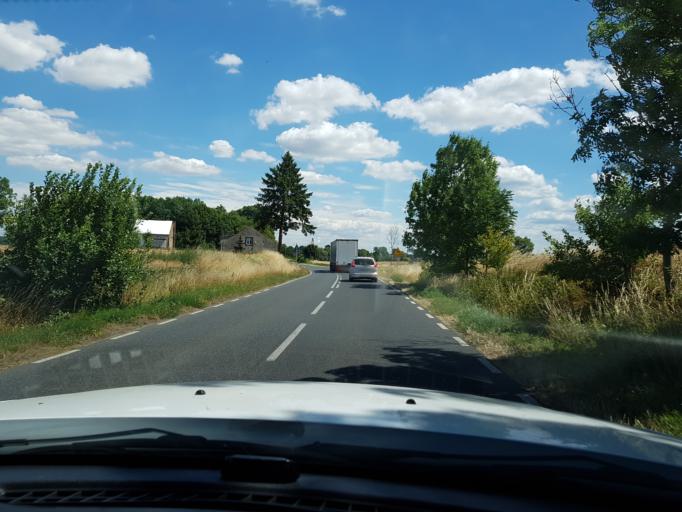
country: PL
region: West Pomeranian Voivodeship
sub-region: Powiat mysliborski
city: Mysliborz
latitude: 52.9064
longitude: 14.9447
